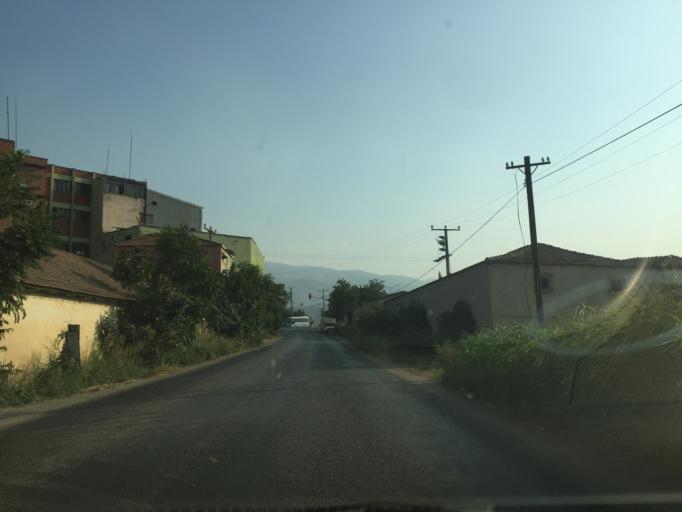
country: TR
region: Manisa
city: Salihli
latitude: 38.4963
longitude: 28.1820
